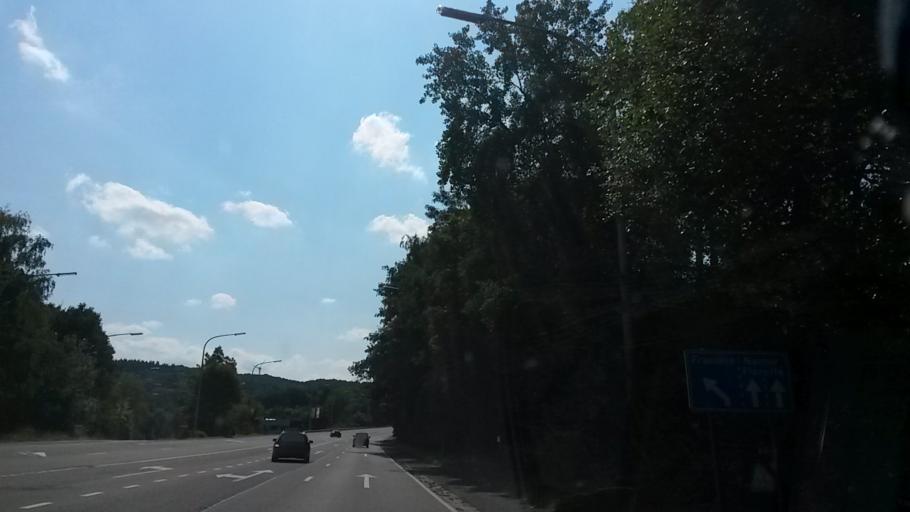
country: BE
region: Wallonia
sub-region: Province de Namur
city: Fosses-la-Ville
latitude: 50.4470
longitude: 4.7038
